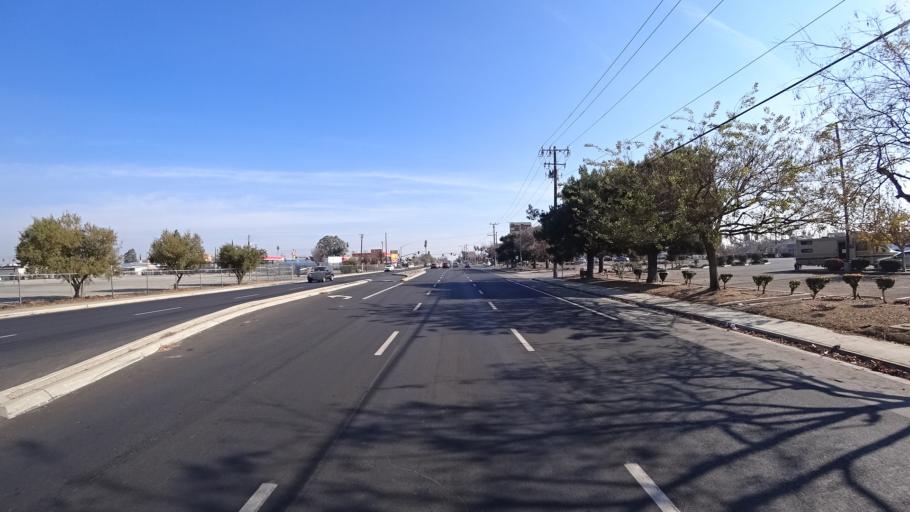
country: US
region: California
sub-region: Kern County
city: Greenfield
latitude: 35.3176
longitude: -119.0232
